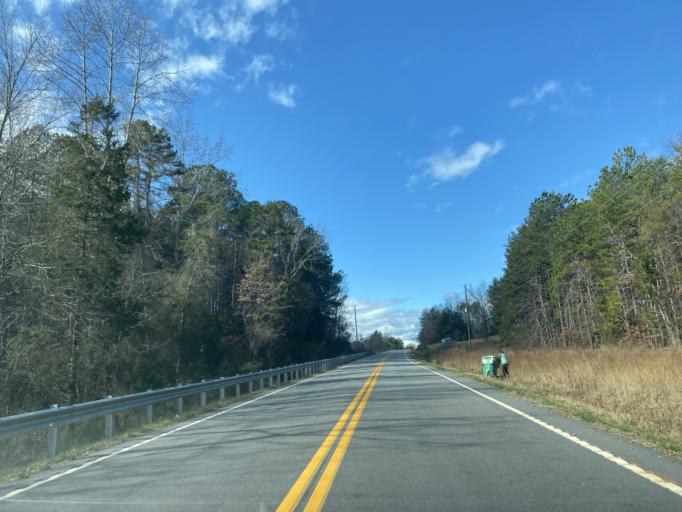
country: US
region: South Carolina
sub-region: Spartanburg County
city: Cowpens
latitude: 35.0955
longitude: -81.7494
